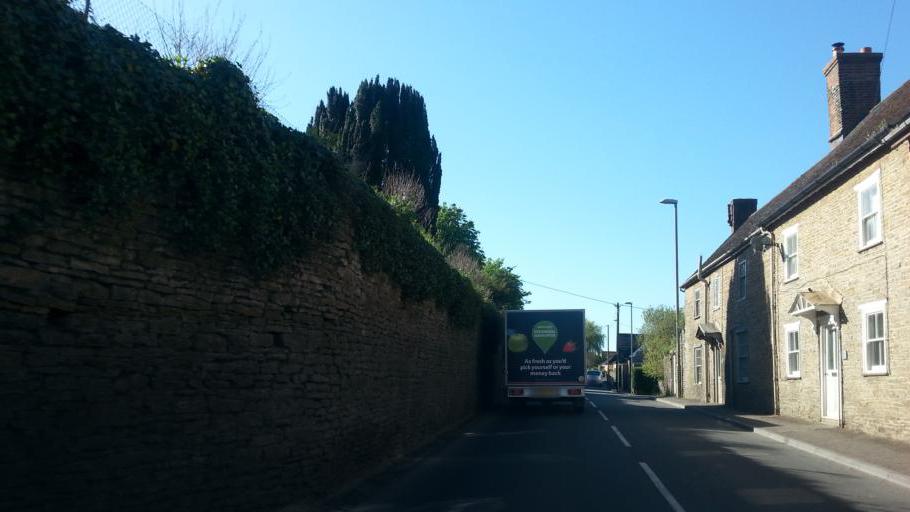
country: GB
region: England
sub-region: Dorset
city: Stalbridge
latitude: 50.9626
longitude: -2.3804
